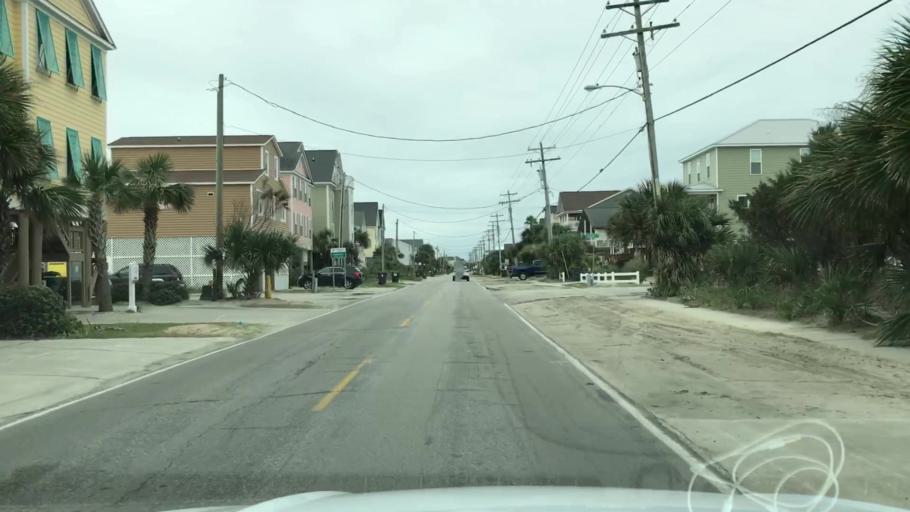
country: US
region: South Carolina
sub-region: Horry County
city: Garden City
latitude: 33.5736
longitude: -79.0015
